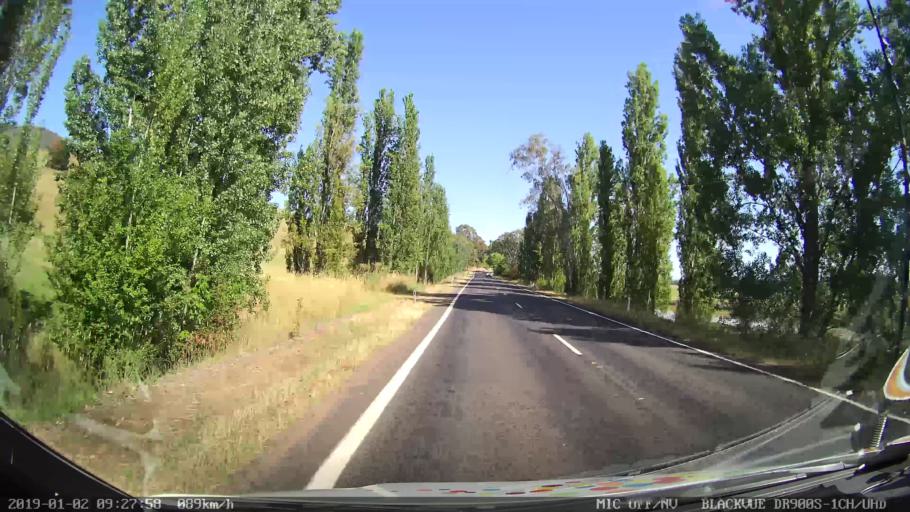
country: AU
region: New South Wales
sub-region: Tumut Shire
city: Tumut
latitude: -35.3562
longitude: 148.2527
